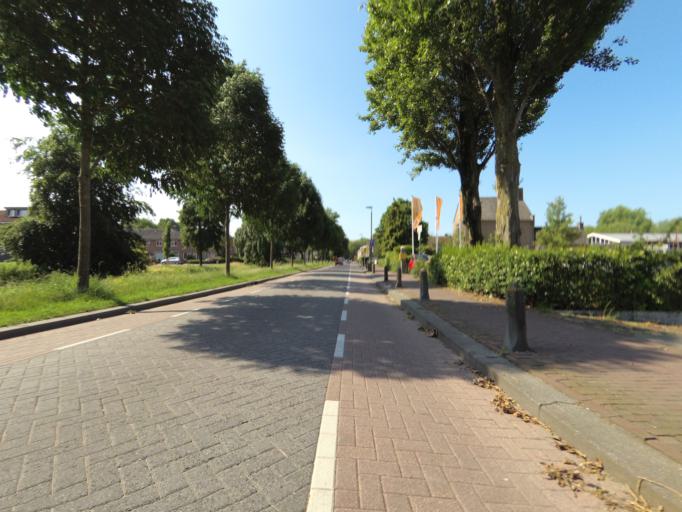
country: NL
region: Utrecht
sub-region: Gemeente Vianen
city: Vianen
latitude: 52.0086
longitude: 5.0989
